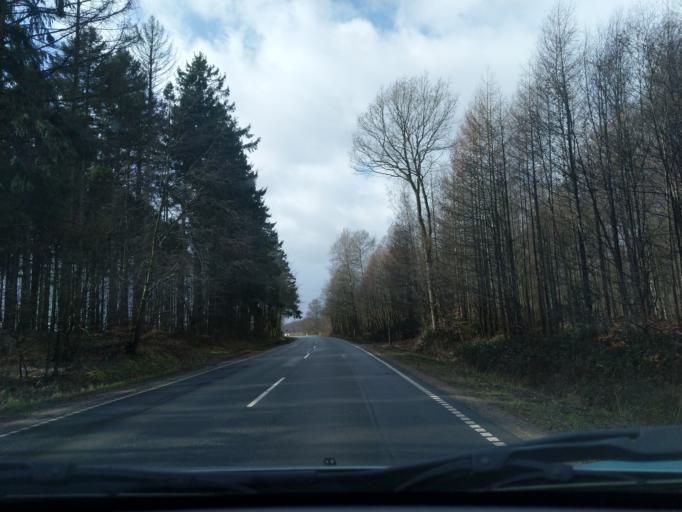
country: DK
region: Zealand
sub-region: Naestved Kommune
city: Fuglebjerg
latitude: 55.3266
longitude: 11.5877
